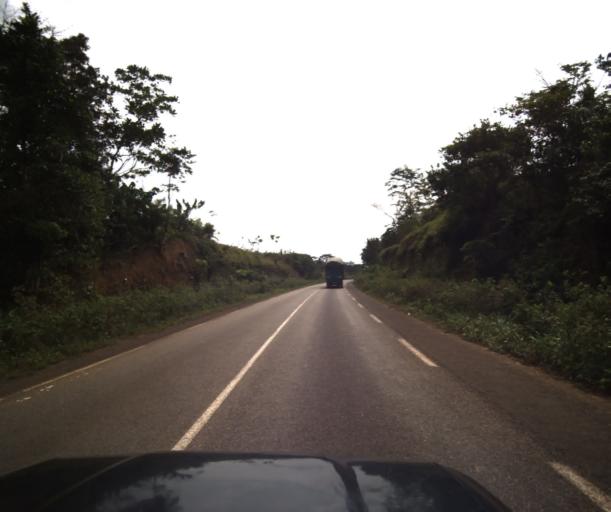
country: CM
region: Littoral
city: Edea
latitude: 3.8164
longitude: 10.3601
